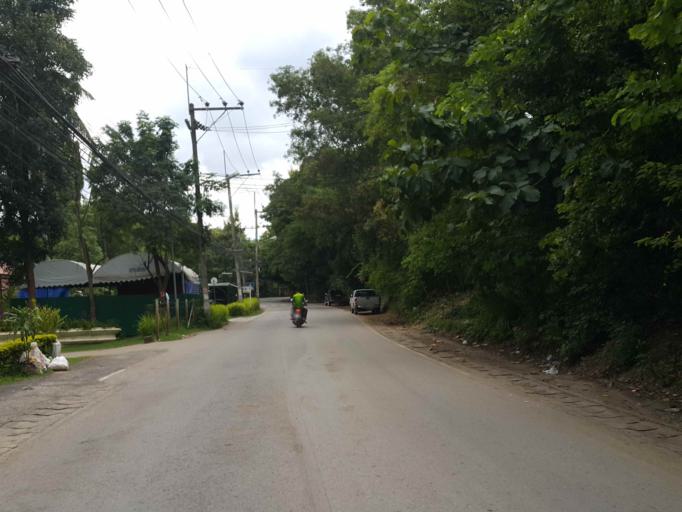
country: TH
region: Chiang Mai
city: San Sai
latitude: 18.9126
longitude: 98.9316
